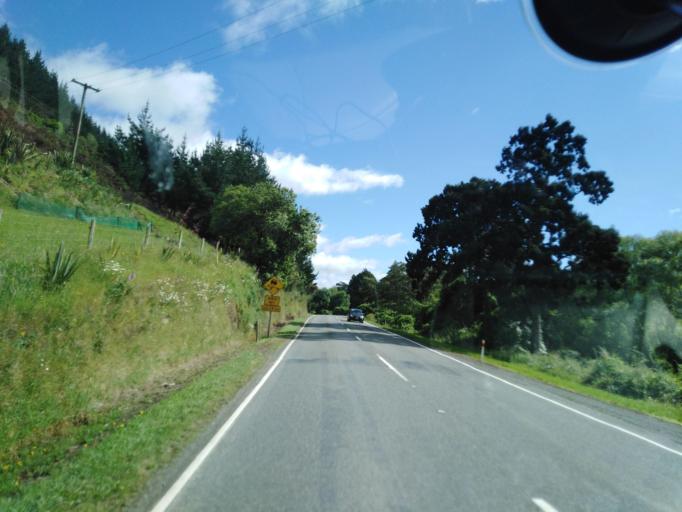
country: NZ
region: Nelson
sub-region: Nelson City
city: Nelson
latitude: -41.2593
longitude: 173.5753
